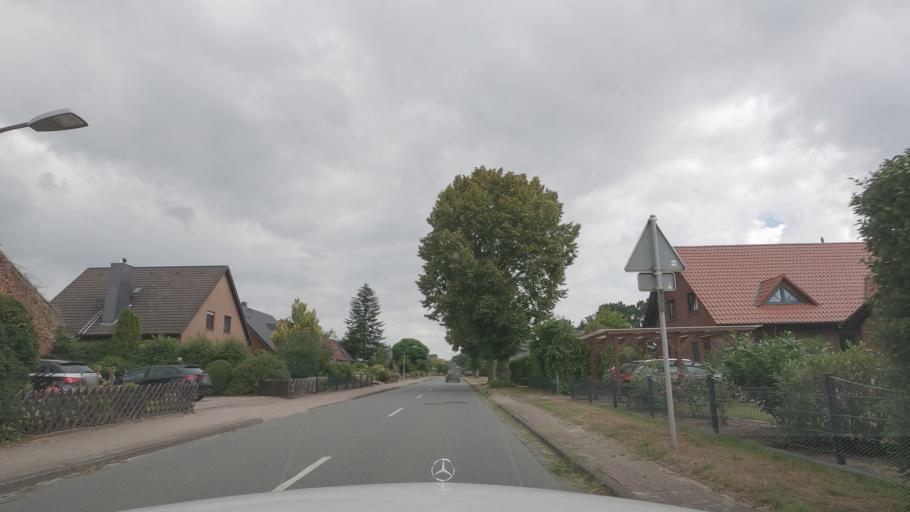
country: DE
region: Lower Saxony
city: Neuenkirchen
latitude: 53.2358
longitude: 8.5275
